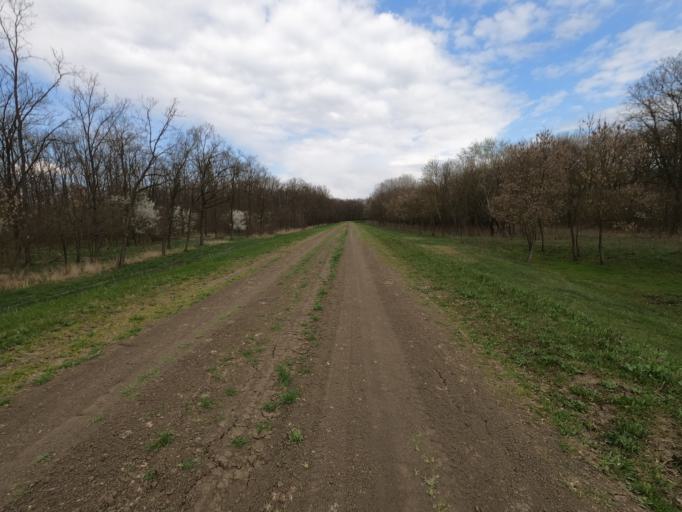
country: HU
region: Jasz-Nagykun-Szolnok
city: Turkeve
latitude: 47.0951
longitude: 20.7805
